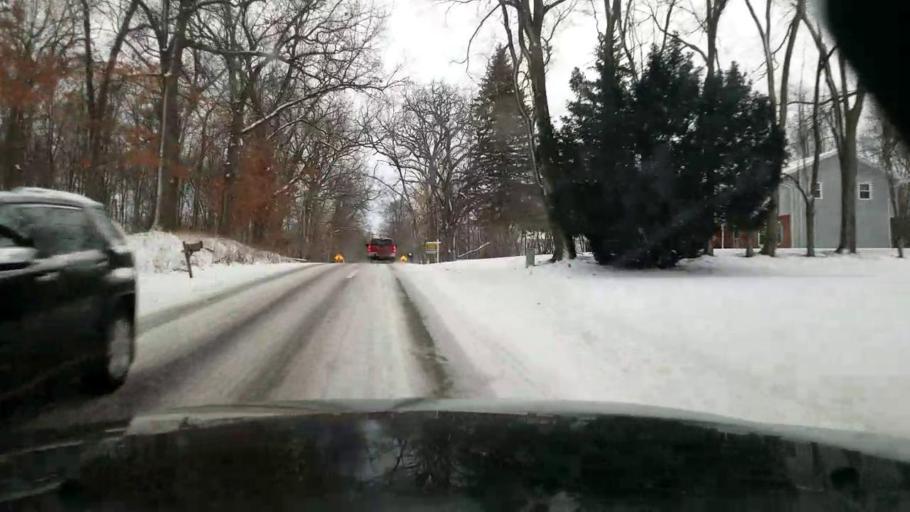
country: US
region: Michigan
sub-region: Jackson County
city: Spring Arbor
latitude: 42.1837
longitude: -84.5009
